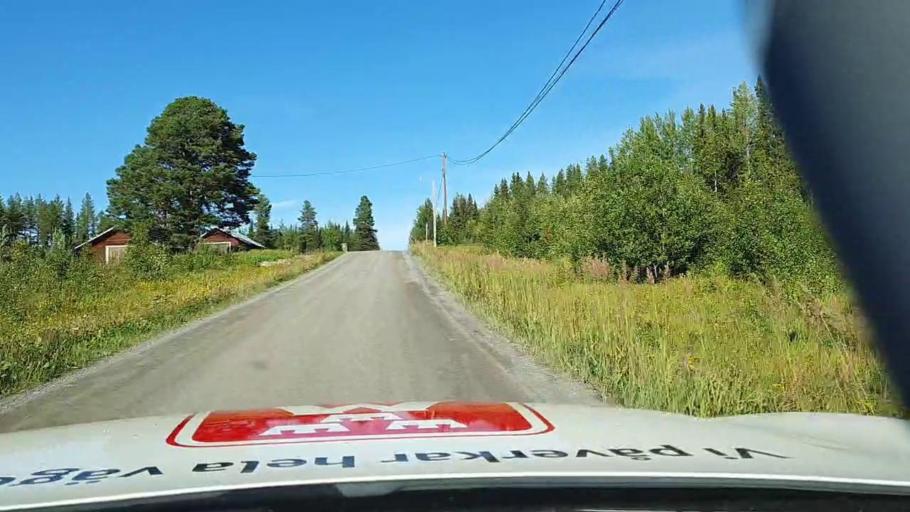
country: SE
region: Jaemtland
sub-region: Krokoms Kommun
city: Krokom
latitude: 63.6828
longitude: 14.6031
